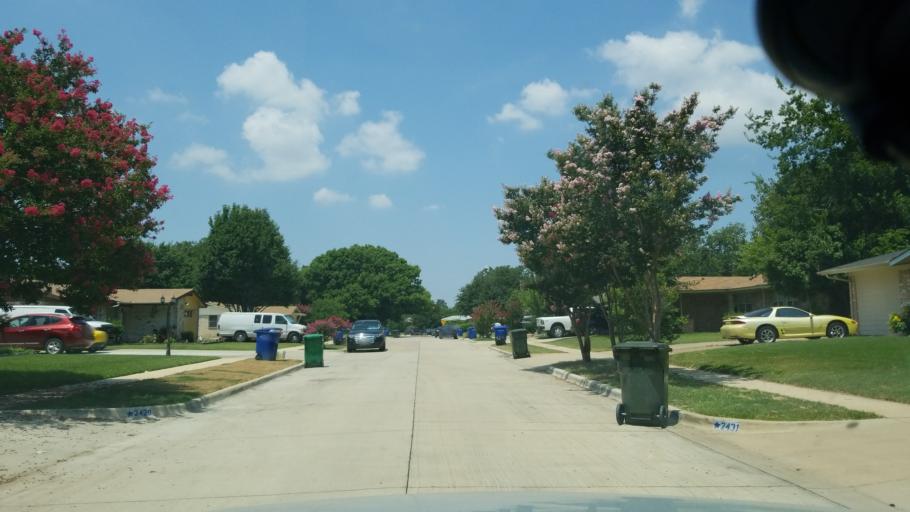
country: US
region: Texas
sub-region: Dallas County
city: Carrollton
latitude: 32.9522
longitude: -96.8736
